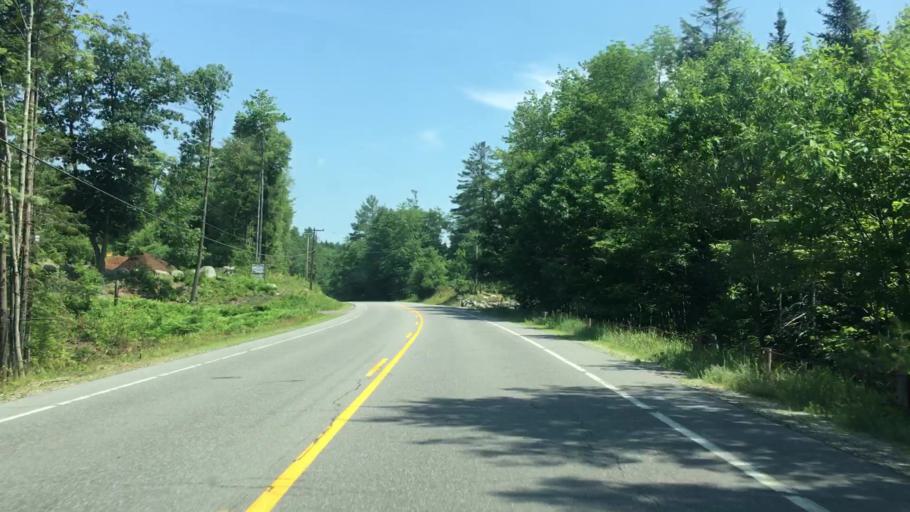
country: US
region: New Hampshire
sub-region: Sullivan County
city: Newport
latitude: 43.4257
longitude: -72.1703
